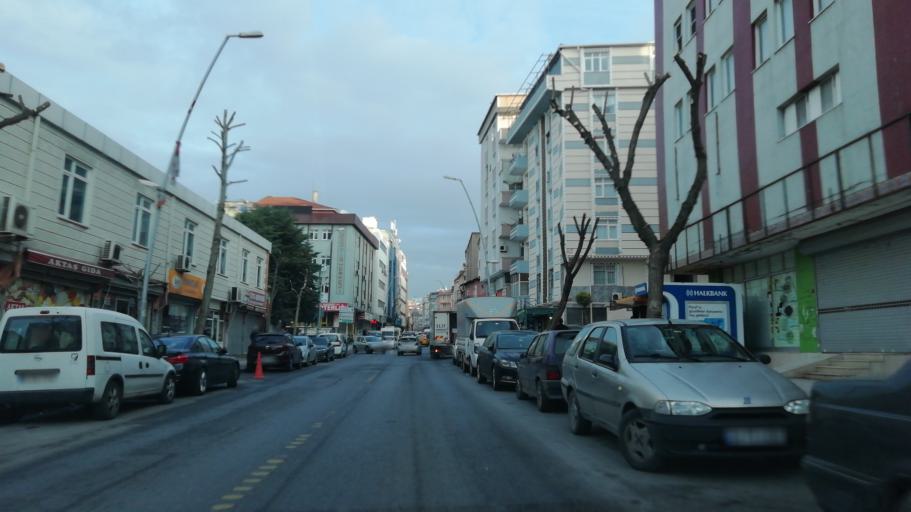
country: TR
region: Istanbul
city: Bahcelievler
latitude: 41.0003
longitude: 28.8270
